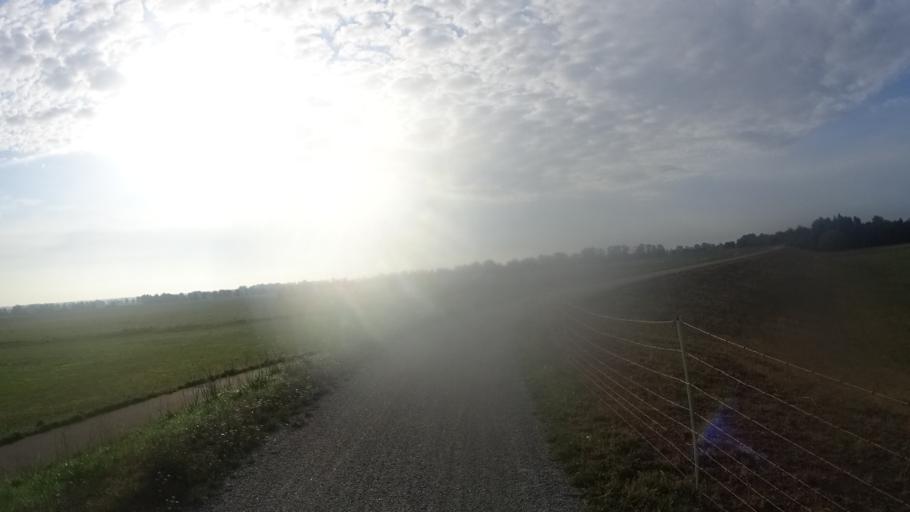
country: DE
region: Brandenburg
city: Lanz
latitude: 53.0517
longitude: 11.5679
